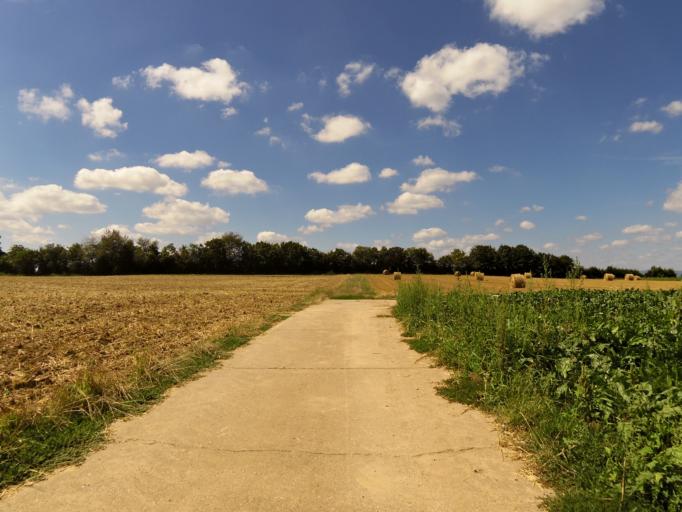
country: DE
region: Rheinland-Pfalz
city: Rulzheim
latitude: 49.1750
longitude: 8.2971
